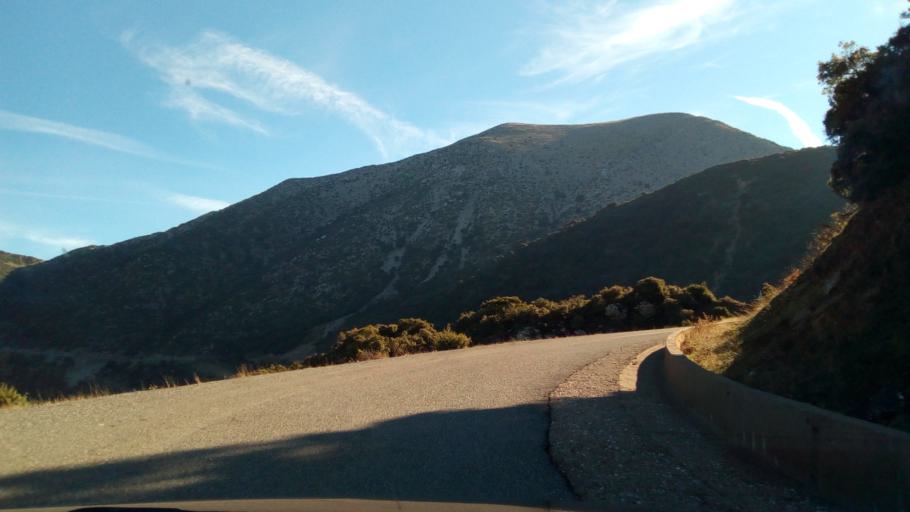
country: GR
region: West Greece
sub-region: Nomos Aitolias kai Akarnanias
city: Nafpaktos
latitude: 38.5097
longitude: 21.8372
